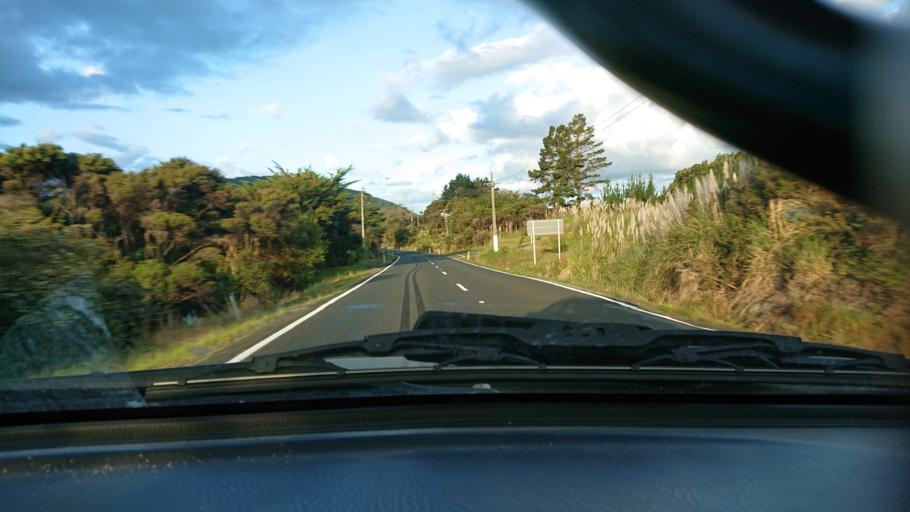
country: NZ
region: Auckland
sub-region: Auckland
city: Parakai
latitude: -36.5102
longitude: 174.4540
